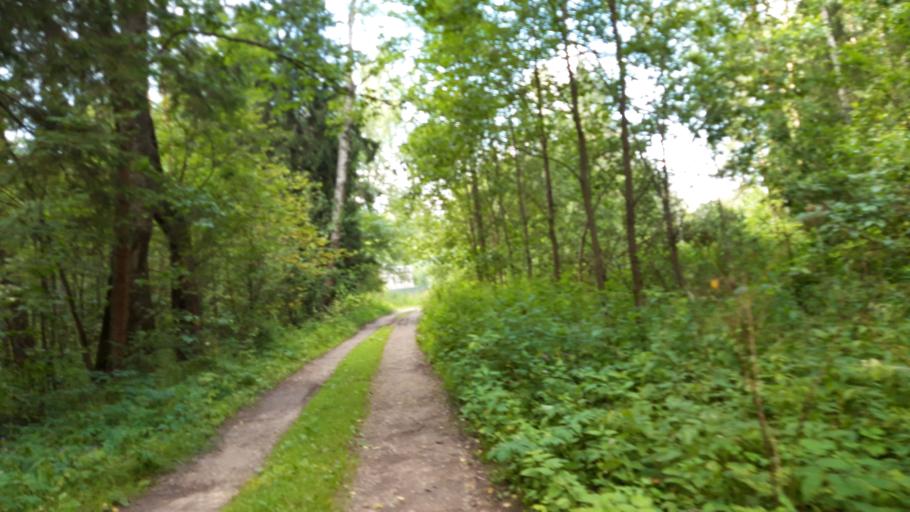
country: RU
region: Tverskaya
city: Konakovo
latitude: 56.6905
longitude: 36.7085
